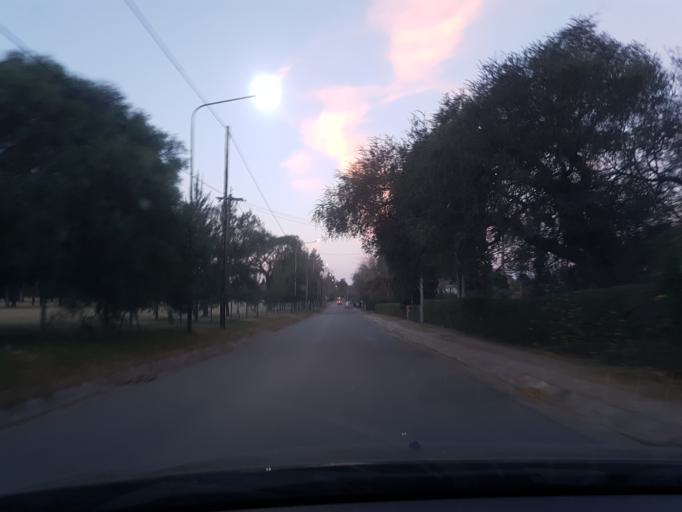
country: AR
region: Cordoba
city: Villa Allende
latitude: -31.2827
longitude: -64.2887
